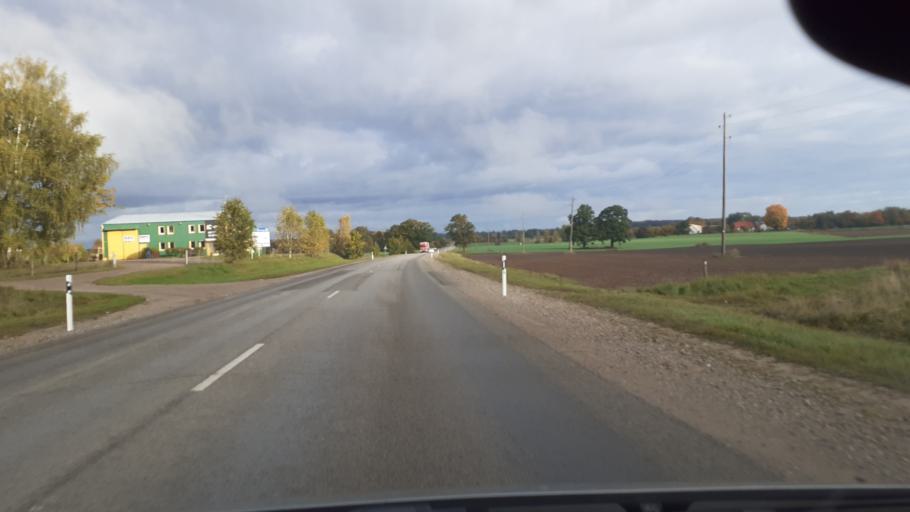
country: LV
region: Kuldigas Rajons
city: Kuldiga
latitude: 56.9717
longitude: 21.9325
